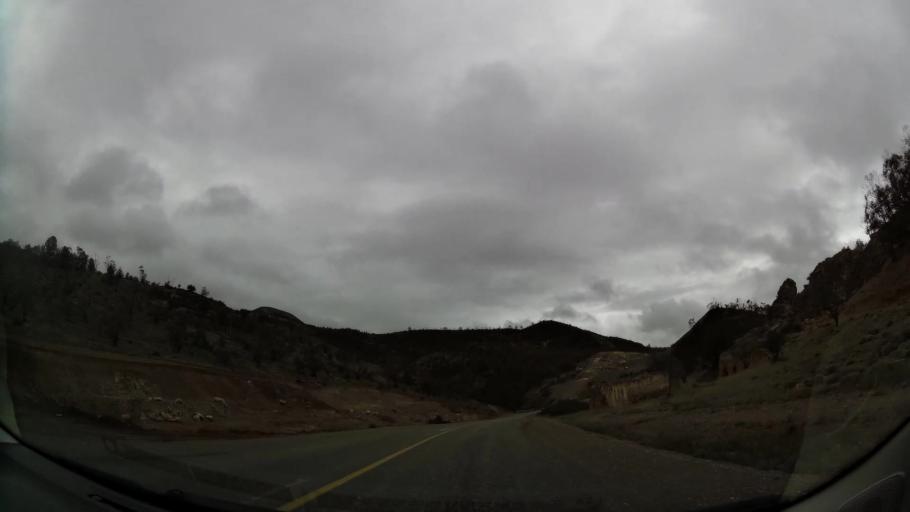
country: MA
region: Taza-Al Hoceima-Taounate
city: Imzourene
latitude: 34.9405
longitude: -3.8084
